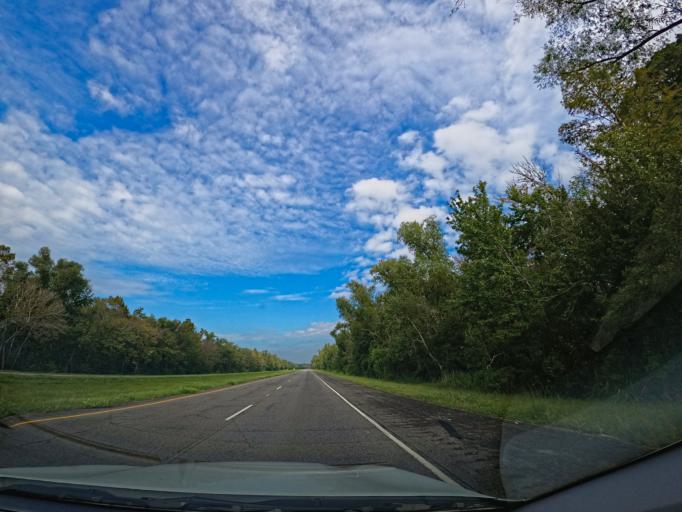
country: US
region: Louisiana
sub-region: Saint Mary Parish
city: Patterson
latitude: 29.7120
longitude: -91.3964
